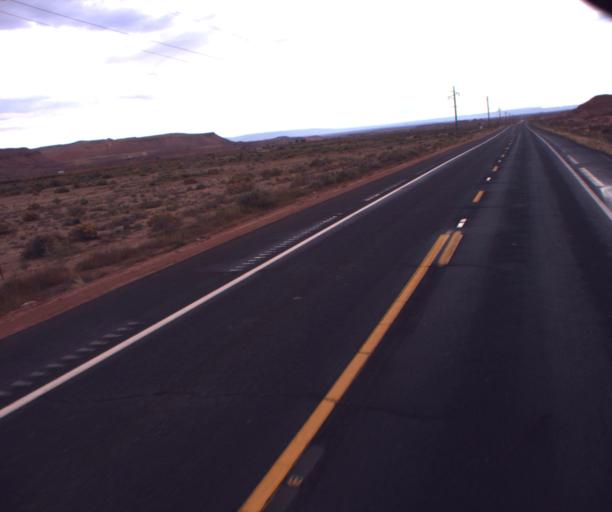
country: US
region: Arizona
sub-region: Coconino County
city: Tuba City
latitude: 36.1068
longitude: -111.2545
